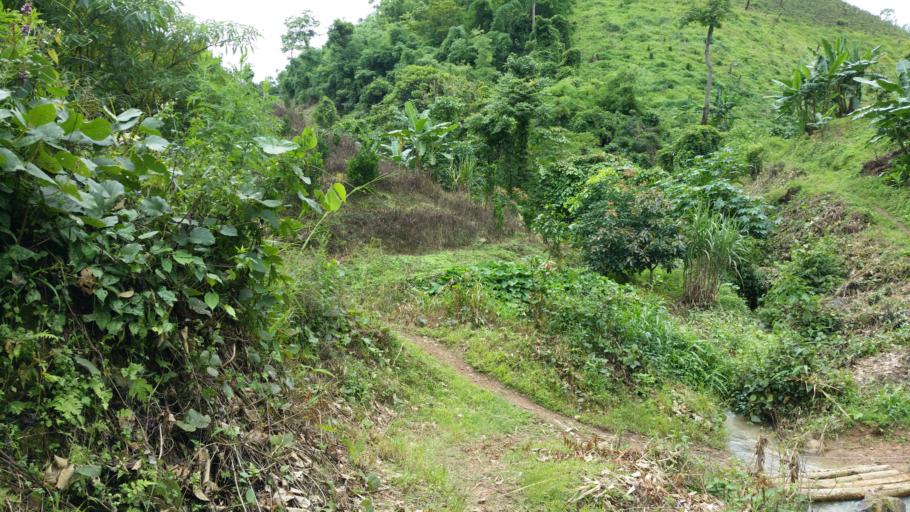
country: MM
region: Mandalay
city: Yamethin
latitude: 20.6219
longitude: 96.5213
